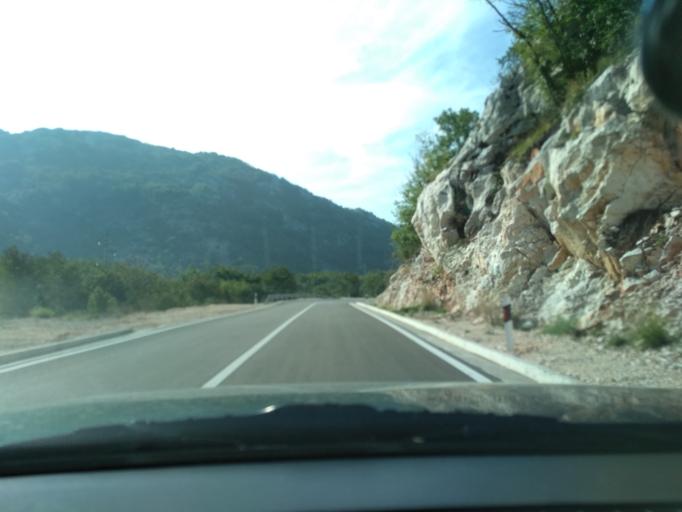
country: ME
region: Cetinje
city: Cetinje
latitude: 42.4278
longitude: 18.8661
